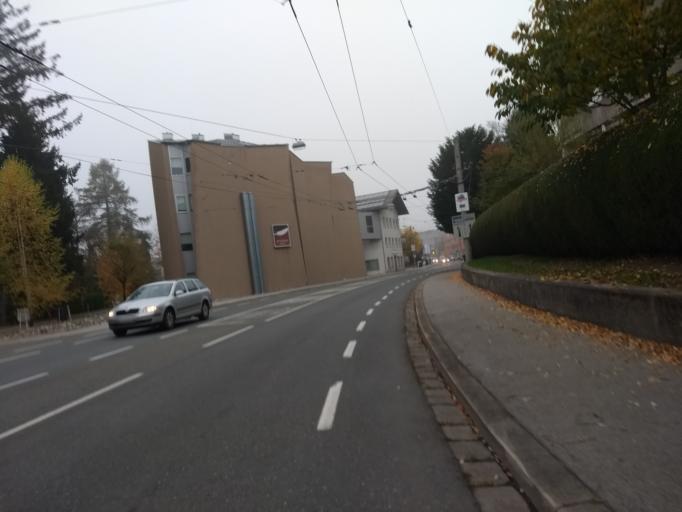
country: AT
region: Salzburg
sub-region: Salzburg Stadt
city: Salzburg
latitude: 47.7998
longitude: 13.0182
